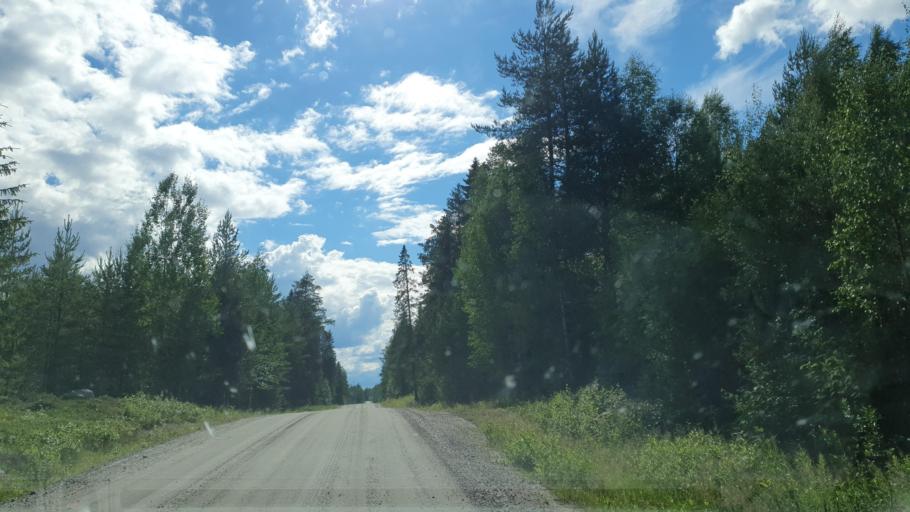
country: FI
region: Kainuu
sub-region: Kehys-Kainuu
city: Kuhmo
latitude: 64.1486
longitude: 29.7217
